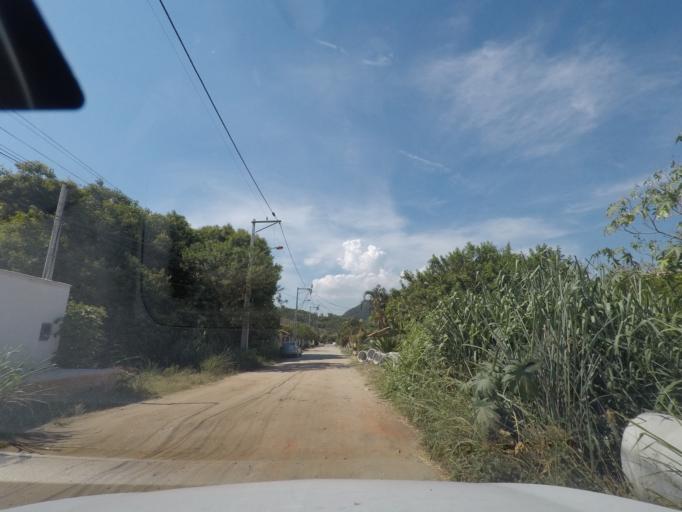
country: BR
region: Rio de Janeiro
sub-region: Niteroi
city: Niteroi
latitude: -22.9590
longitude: -42.9685
